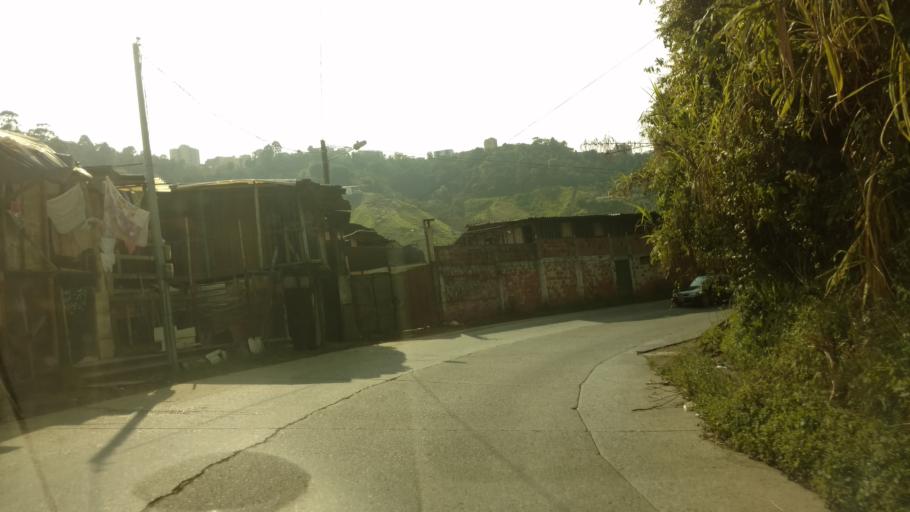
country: CO
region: Caldas
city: Manizales
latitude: 5.0810
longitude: -75.5151
